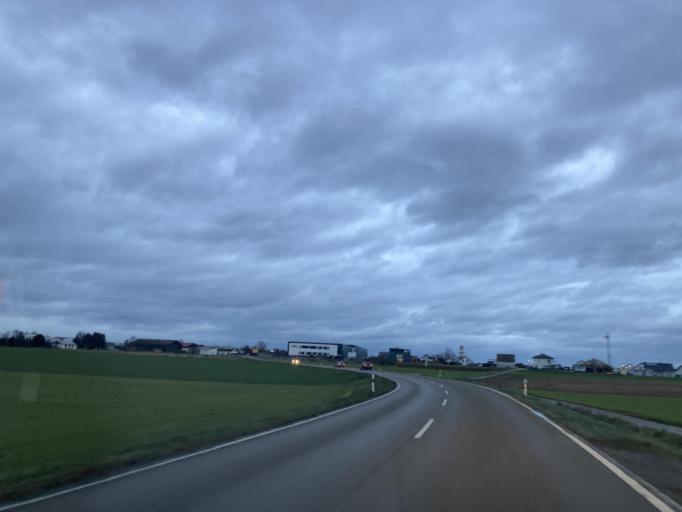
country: DE
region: Baden-Wuerttemberg
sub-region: Tuebingen Region
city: Rammingen
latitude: 48.5140
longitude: 10.1620
